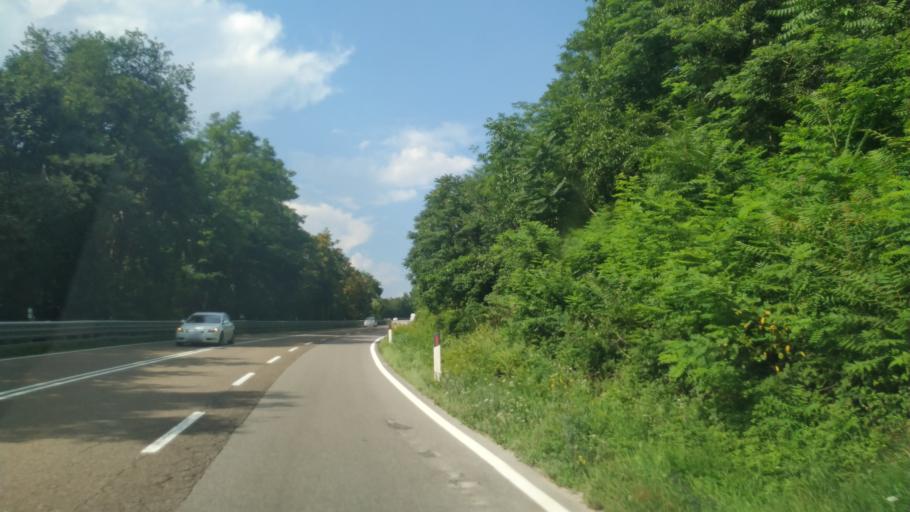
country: IT
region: Trentino-Alto Adige
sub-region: Provincia di Trento
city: Denno
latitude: 46.2848
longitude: 11.0624
